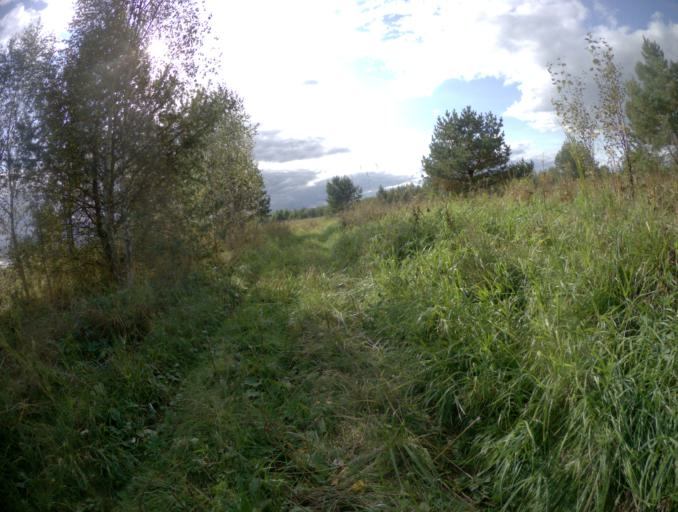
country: RU
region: Vladimir
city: Ivanishchi
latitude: 55.8528
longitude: 40.3992
